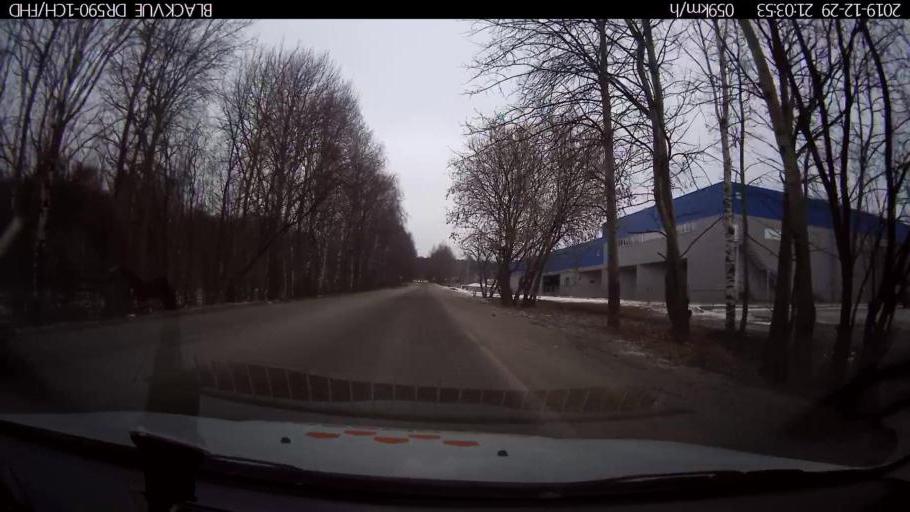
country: RU
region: Nizjnij Novgorod
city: Afonino
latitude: 56.1988
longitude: 44.0050
